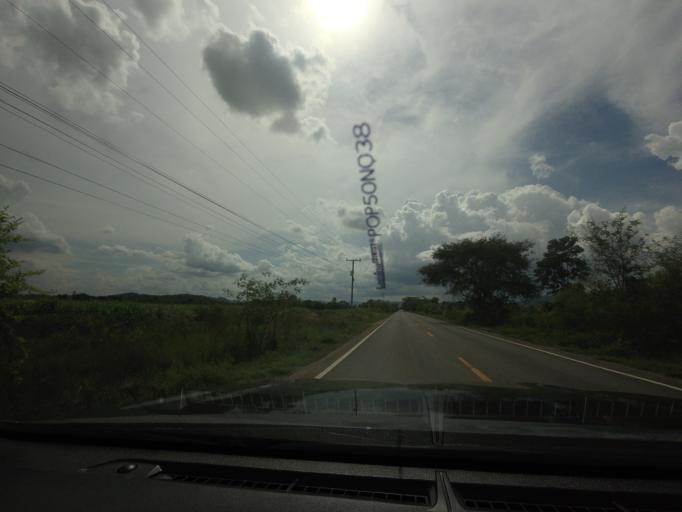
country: TH
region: Kanchanaburi
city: Bo Phloi
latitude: 14.1663
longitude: 99.4540
